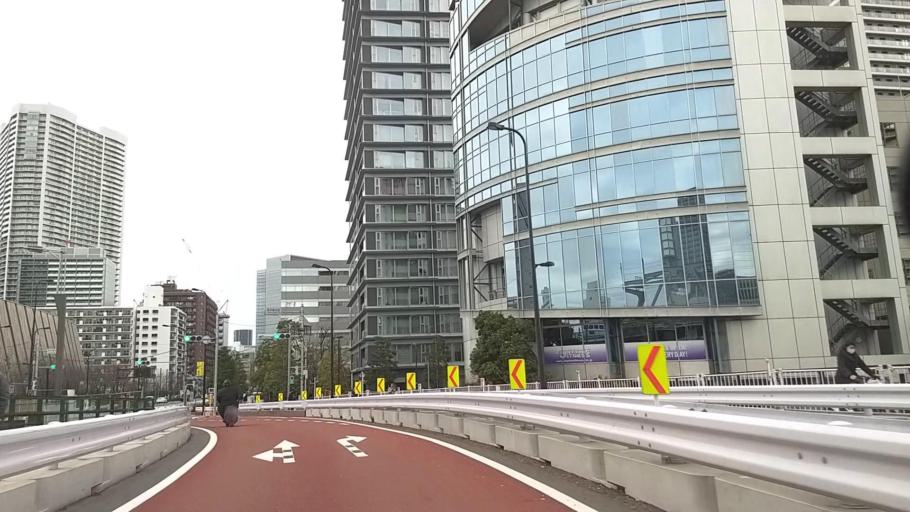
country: JP
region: Tokyo
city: Tokyo
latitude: 35.6368
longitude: 139.7468
